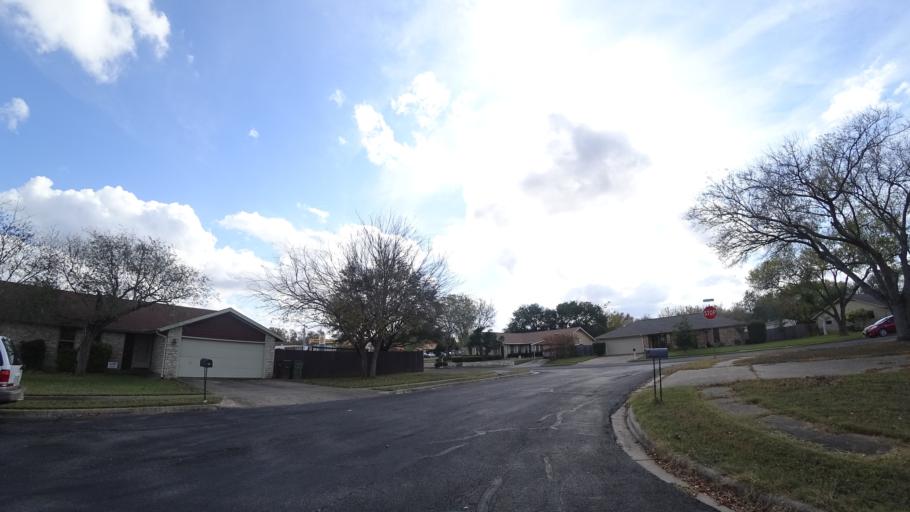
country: US
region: Texas
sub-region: Williamson County
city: Brushy Creek
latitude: 30.5151
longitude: -97.7357
